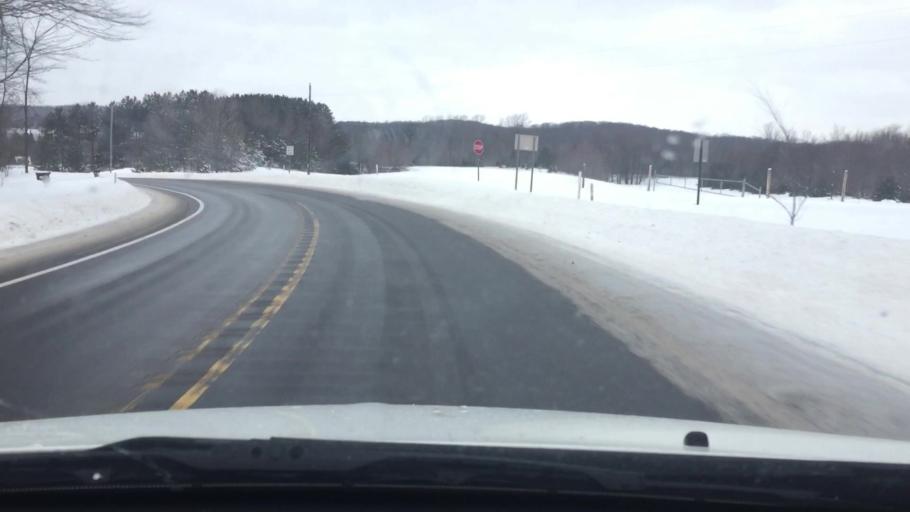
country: US
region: Michigan
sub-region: Charlevoix County
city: East Jordan
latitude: 45.1033
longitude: -85.0313
